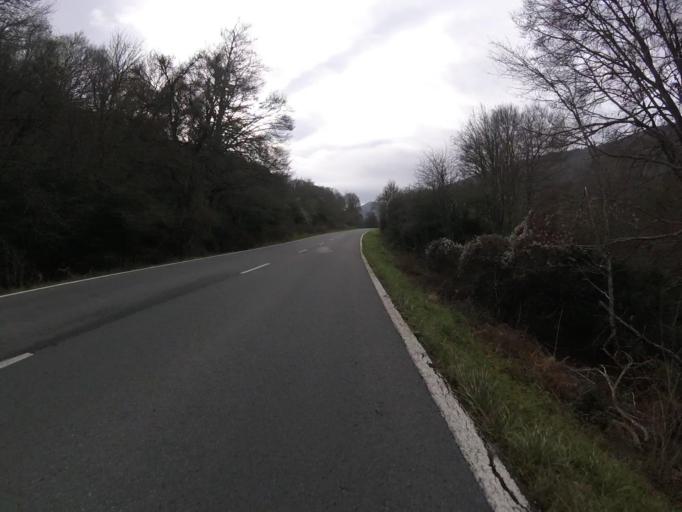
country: ES
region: Navarre
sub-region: Provincia de Navarra
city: Lezaun
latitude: 42.8302
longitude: -2.0278
